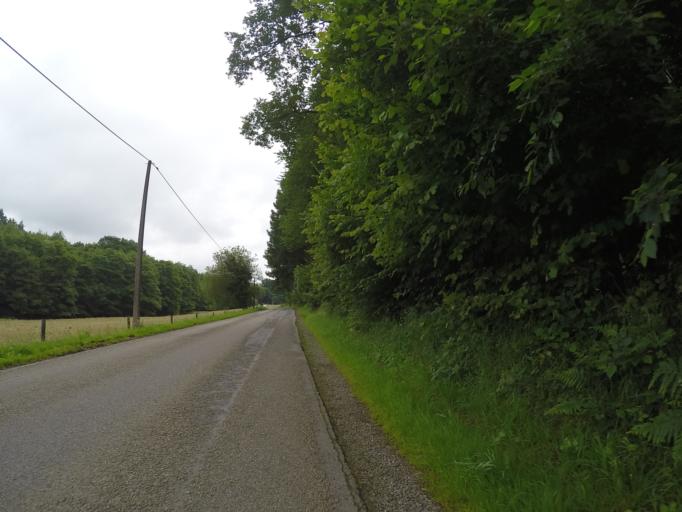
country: BE
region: Wallonia
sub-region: Province de Namur
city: Assesse
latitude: 50.3410
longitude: 4.9607
